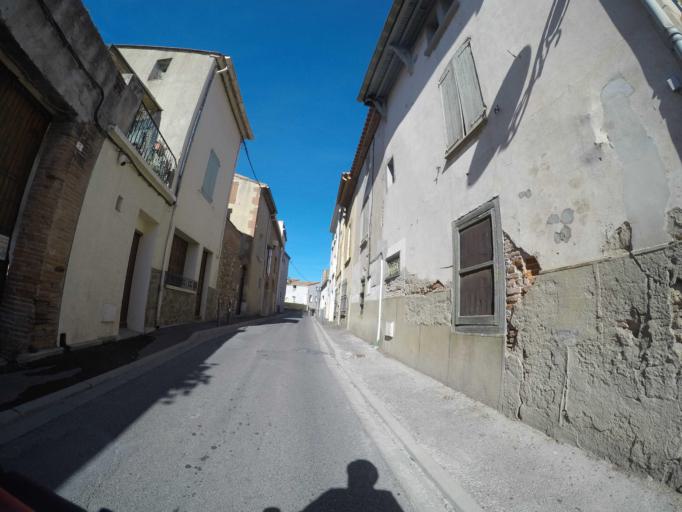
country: FR
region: Languedoc-Roussillon
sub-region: Departement des Pyrenees-Orientales
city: Ponteilla
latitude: 42.6267
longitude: 2.8138
